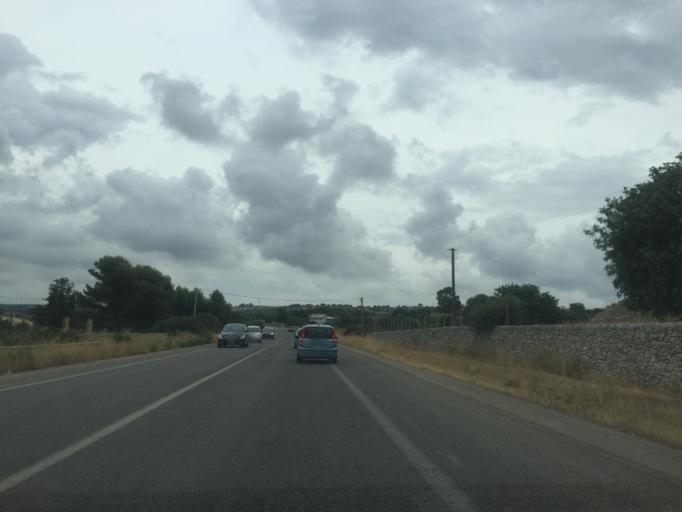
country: IT
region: Sicily
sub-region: Ragusa
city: Marina di Ragusa
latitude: 36.8341
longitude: 14.5917
